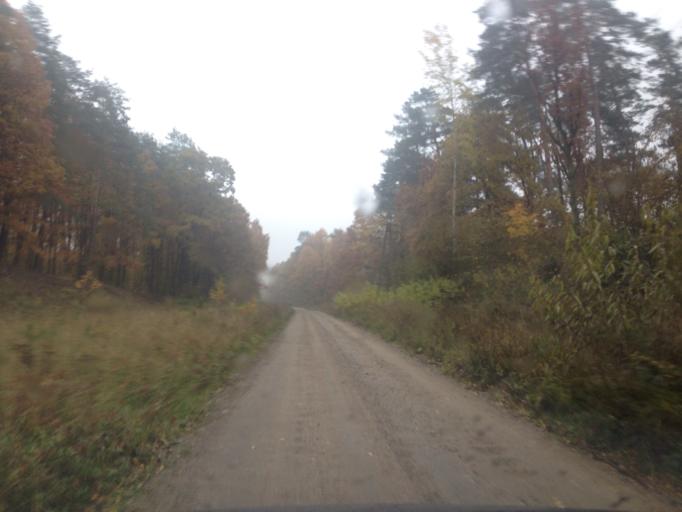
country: PL
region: Kujawsko-Pomorskie
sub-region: Powiat brodnicki
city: Gorzno
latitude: 53.2404
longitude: 19.6837
